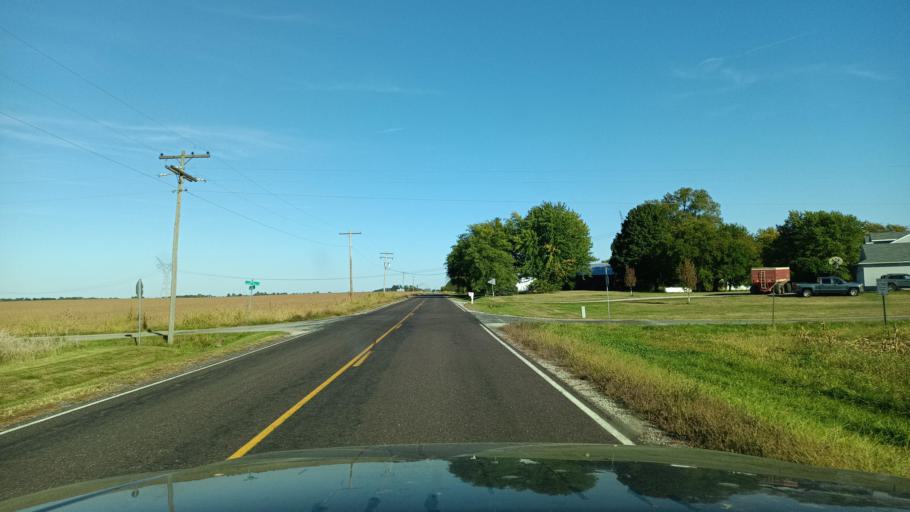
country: US
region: Illinois
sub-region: De Witt County
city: Clinton
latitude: 40.2315
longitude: -88.9957
